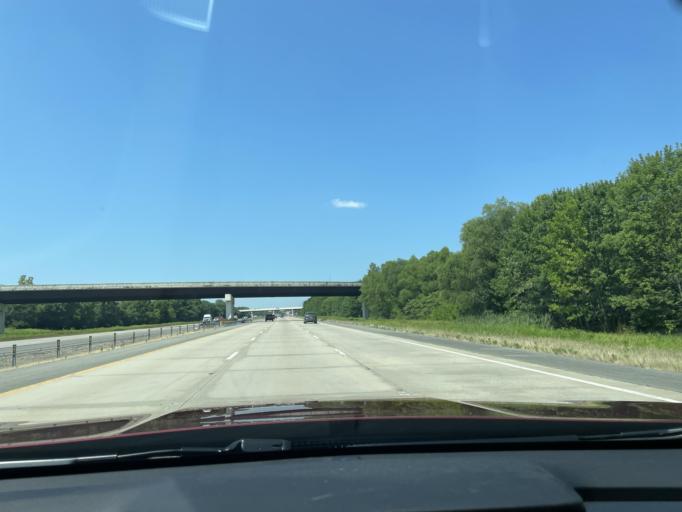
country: US
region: Arkansas
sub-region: Pulaski County
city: Gravel Ridge
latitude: 34.8449
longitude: -92.1525
